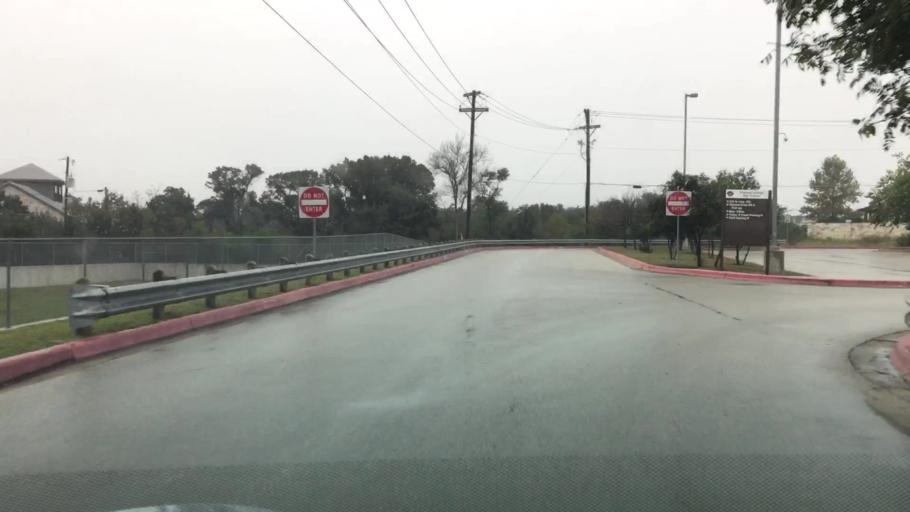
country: US
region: Texas
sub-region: Hays County
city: Dripping Springs
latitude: 30.1970
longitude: -98.0994
